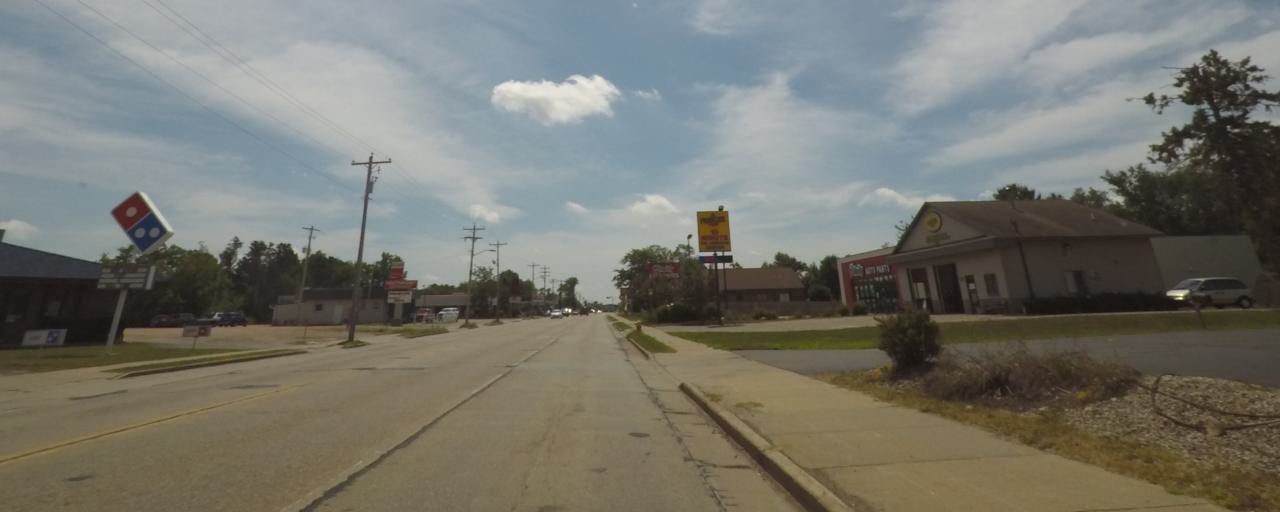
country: US
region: Wisconsin
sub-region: Portage County
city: Whiting
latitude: 44.5067
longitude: -89.5684
